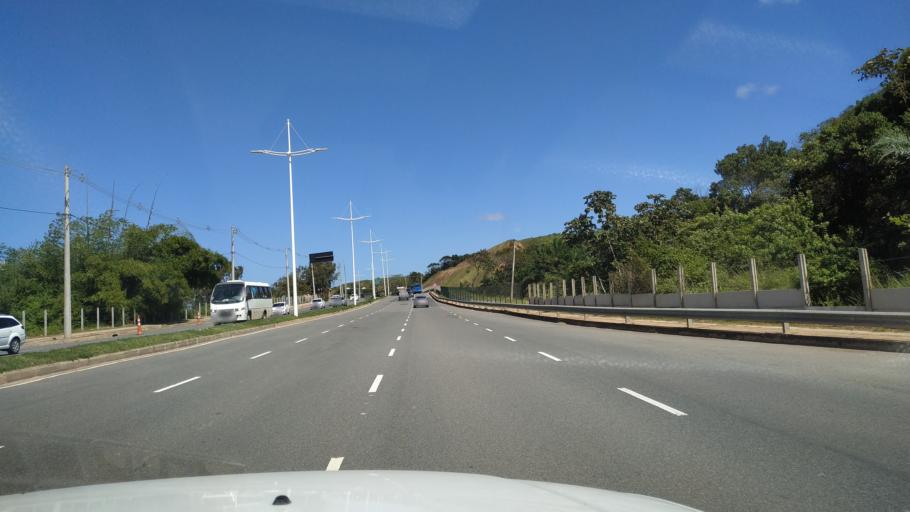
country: BR
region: Bahia
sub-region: Lauro De Freitas
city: Lauro de Freitas
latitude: -12.9318
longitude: -38.3827
